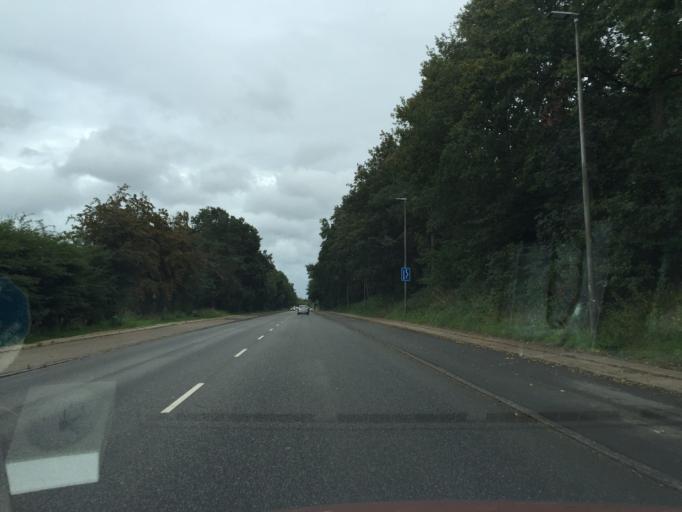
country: DK
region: South Denmark
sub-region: Kolding Kommune
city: Kolding
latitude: 55.4860
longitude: 9.4903
